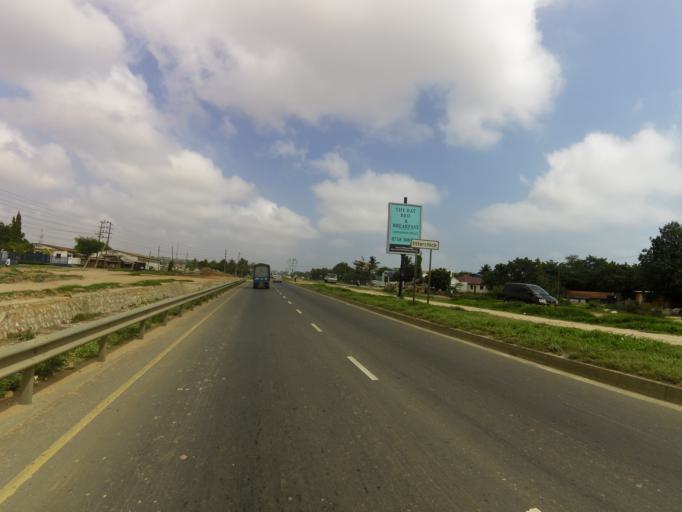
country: TZ
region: Dar es Salaam
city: Magomeni
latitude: -6.7109
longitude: 39.2094
